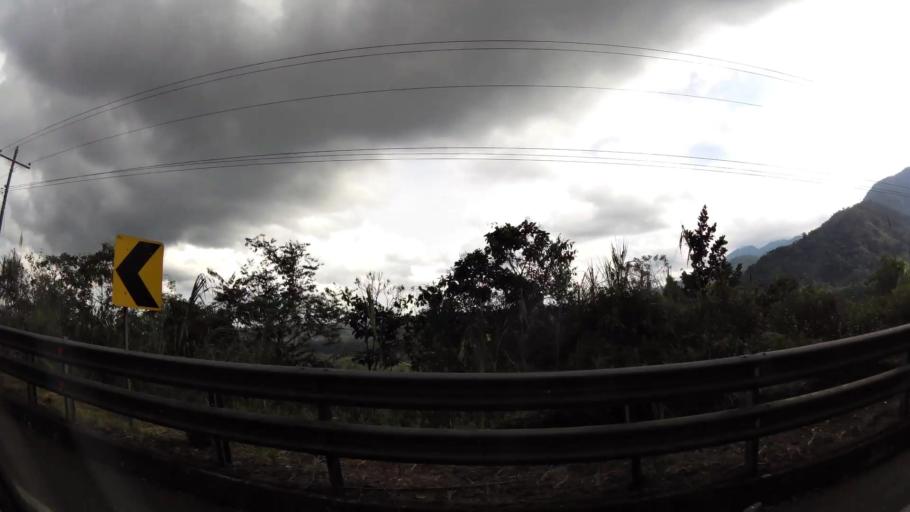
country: EC
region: Pastaza
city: Puyo
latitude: -1.4493
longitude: -78.1390
